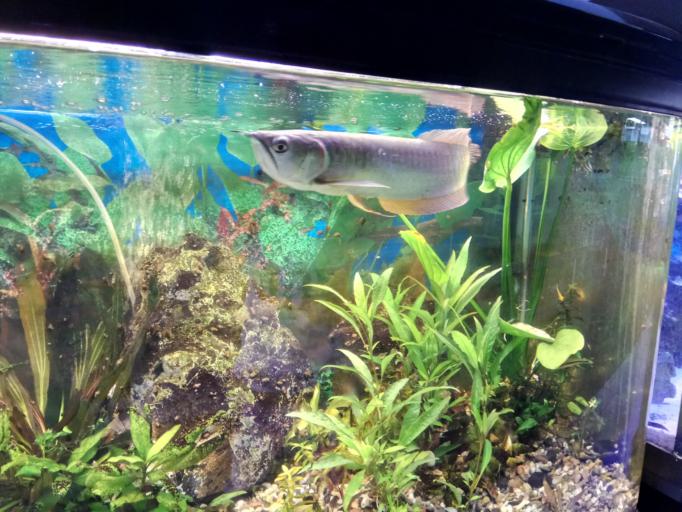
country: CZ
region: Moravskoslezsky
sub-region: Okres Frydek-Mistek
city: Frydek-Mistek
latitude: 49.6853
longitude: 18.3479
